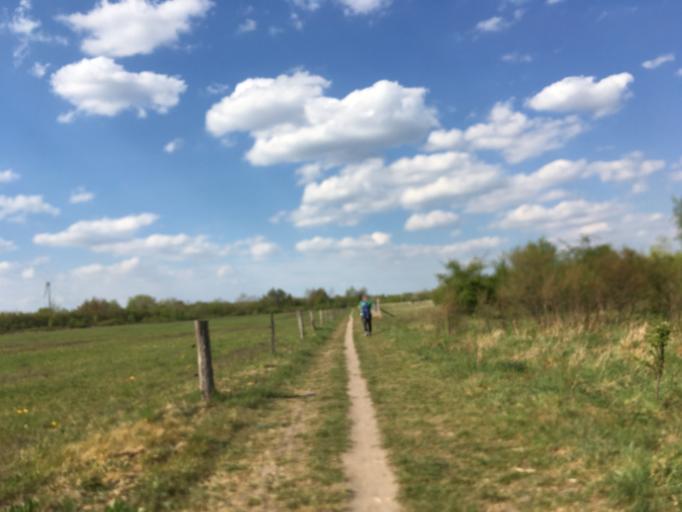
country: DE
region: Berlin
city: Wartenberg
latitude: 52.5824
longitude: 13.5119
